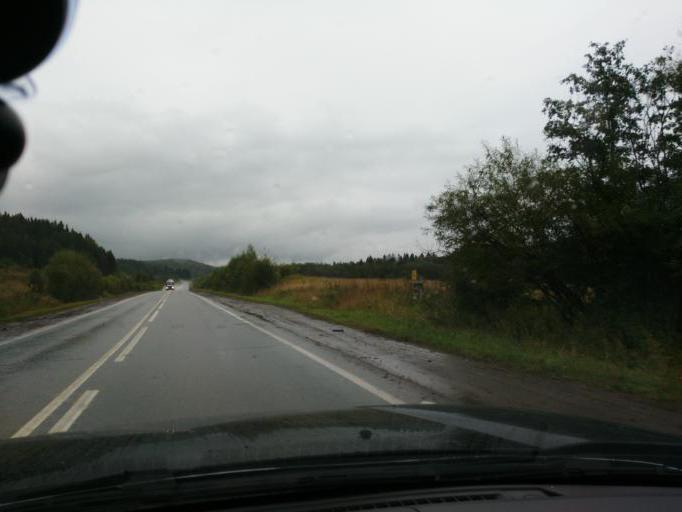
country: RU
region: Perm
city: Yugo-Kamskiy
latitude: 57.7234
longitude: 55.6738
